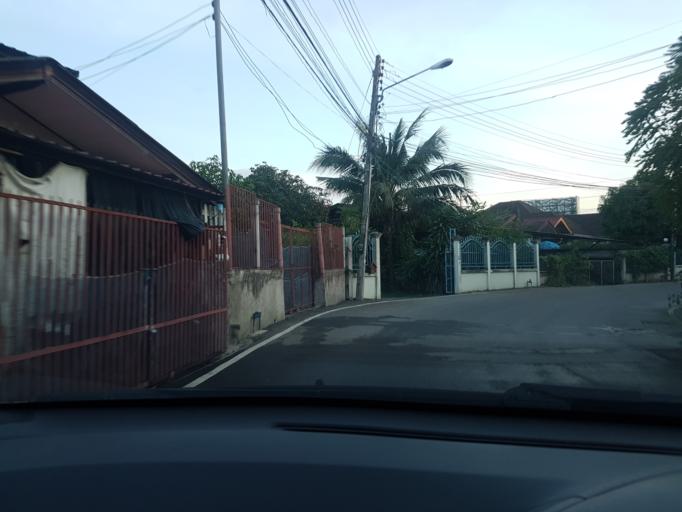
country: TH
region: Chiang Mai
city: San Sai
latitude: 18.8317
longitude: 99.0438
